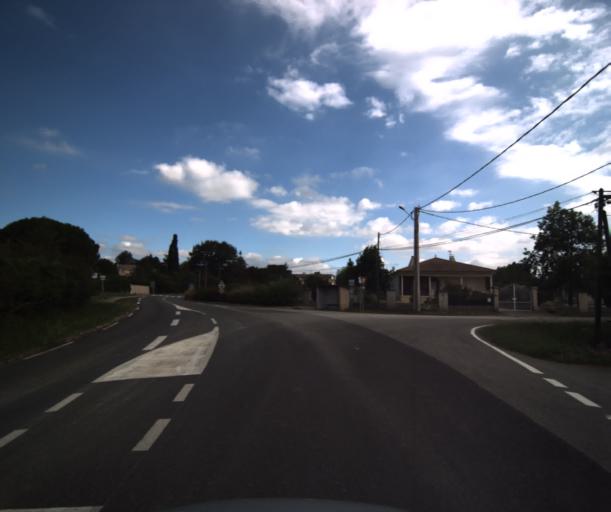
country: FR
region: Midi-Pyrenees
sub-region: Departement de la Haute-Garonne
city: Lacasse
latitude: 43.4016
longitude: 1.2583
